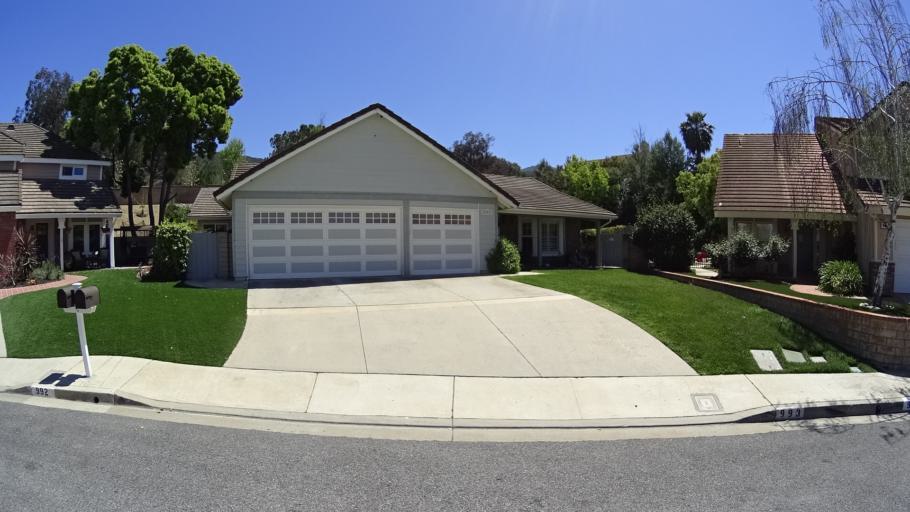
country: US
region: California
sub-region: Ventura County
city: Casa Conejo
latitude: 34.1582
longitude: -118.9493
